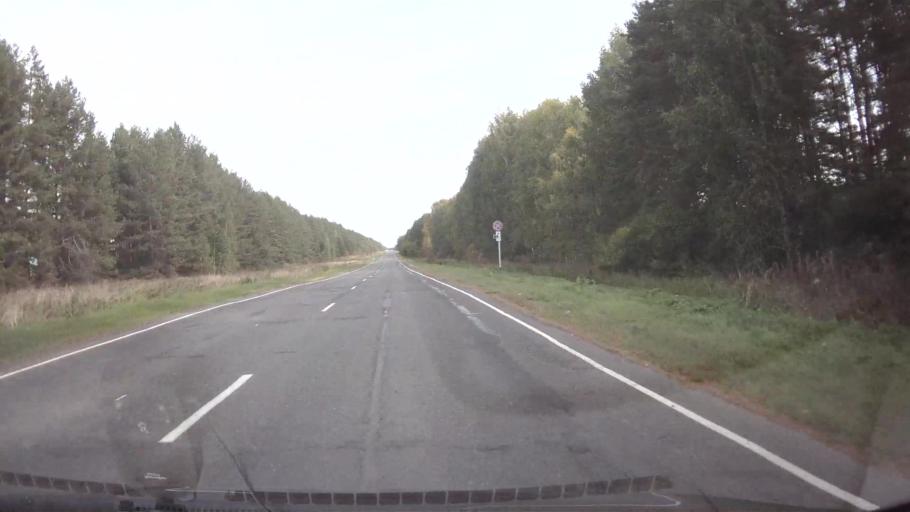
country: RU
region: Mariy-El
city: Kuzhener
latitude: 56.8233
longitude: 48.7203
